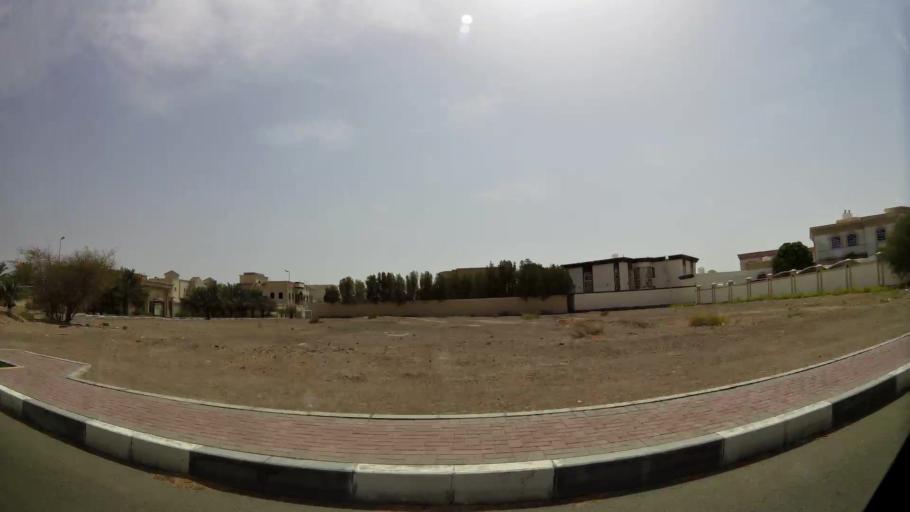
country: AE
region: Abu Dhabi
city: Al Ain
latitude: 24.1692
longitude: 55.6745
